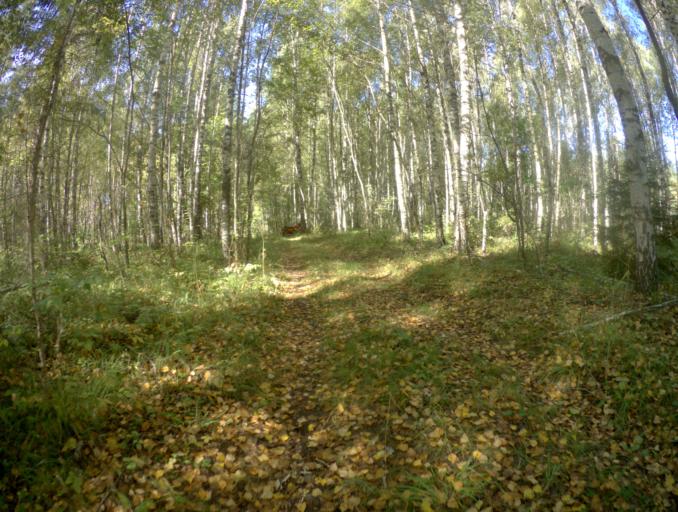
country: RU
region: Vladimir
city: Nikologory
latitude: 56.1087
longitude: 41.9039
